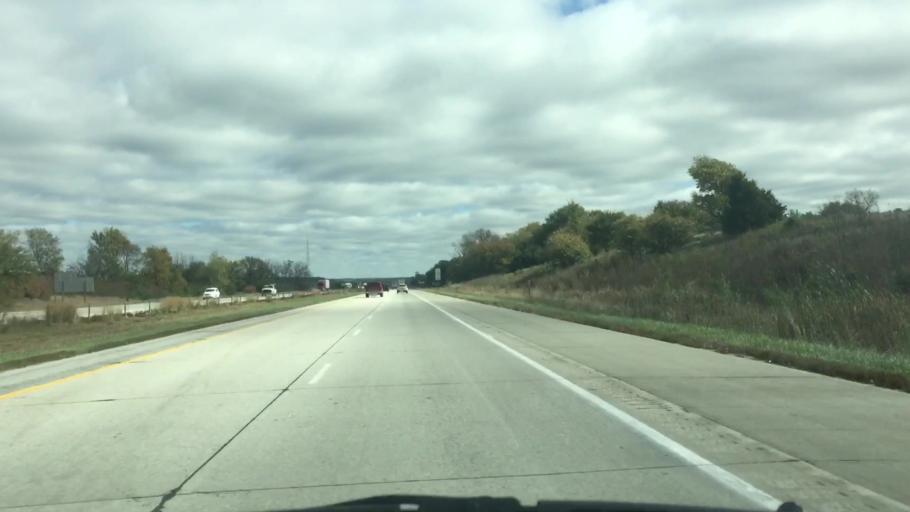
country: US
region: Iowa
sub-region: Polk County
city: Mitchellville
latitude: 41.6804
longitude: -93.3611
